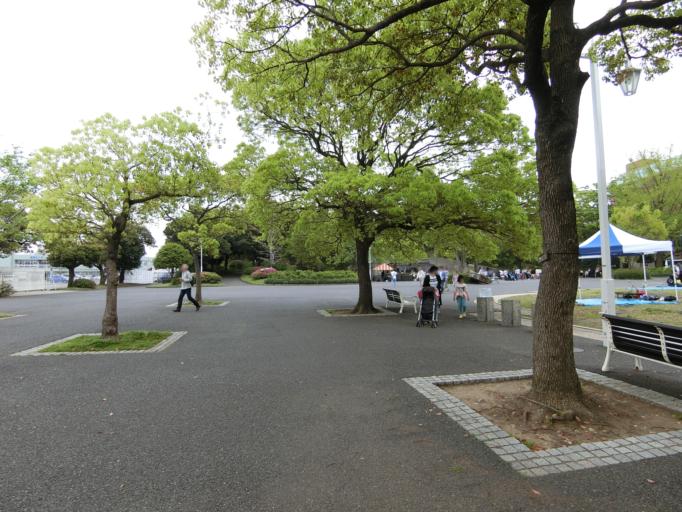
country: JP
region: Kanagawa
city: Yokohama
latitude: 35.4446
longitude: 139.6515
